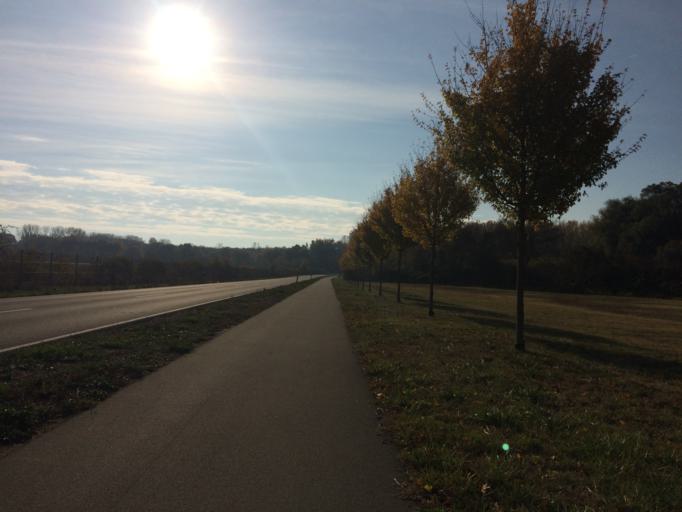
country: DE
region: Baden-Wuerttemberg
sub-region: Karlsruhe Region
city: Oberhausen-Rheinhausen
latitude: 49.2975
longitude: 8.4531
